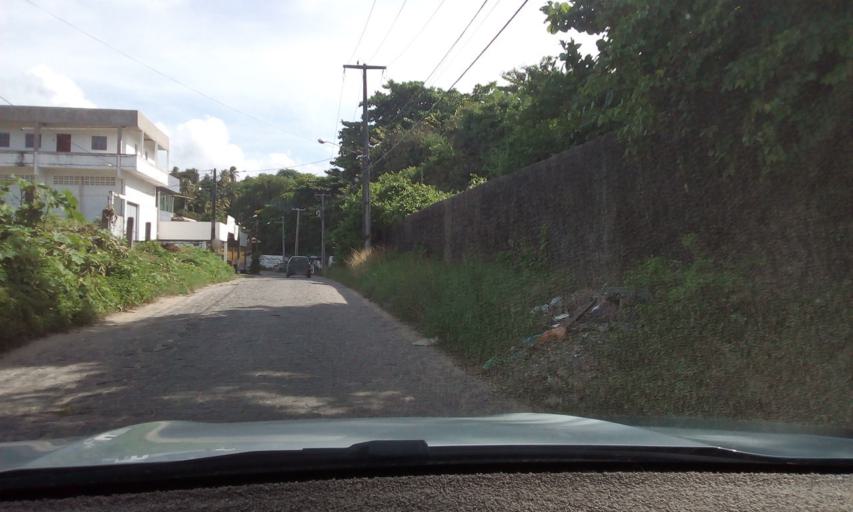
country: BR
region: Paraiba
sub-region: Joao Pessoa
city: Joao Pessoa
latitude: -7.1330
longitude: -34.8875
